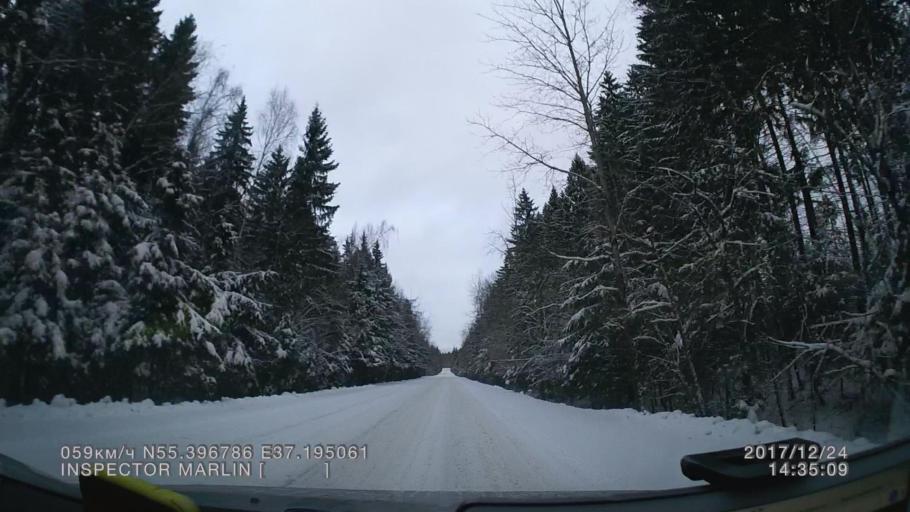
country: RU
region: Moskovskaya
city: Troitsk
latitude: 55.3968
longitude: 37.1951
